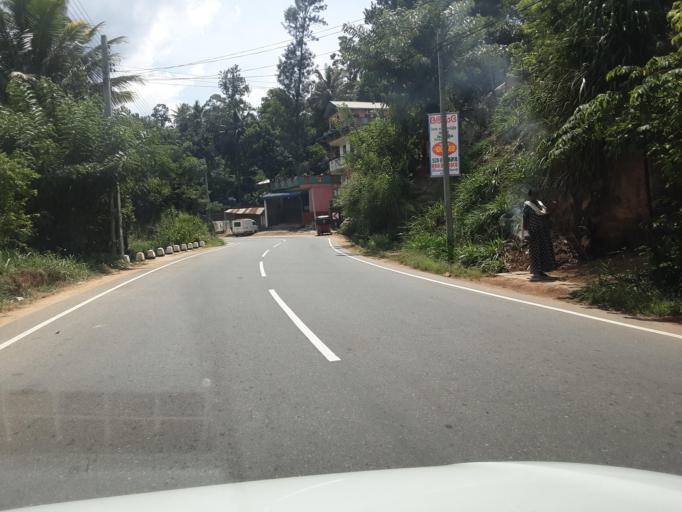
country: LK
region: Central
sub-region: Nuwara Eliya District
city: Nuwara Eliya
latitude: 6.9236
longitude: 80.8993
